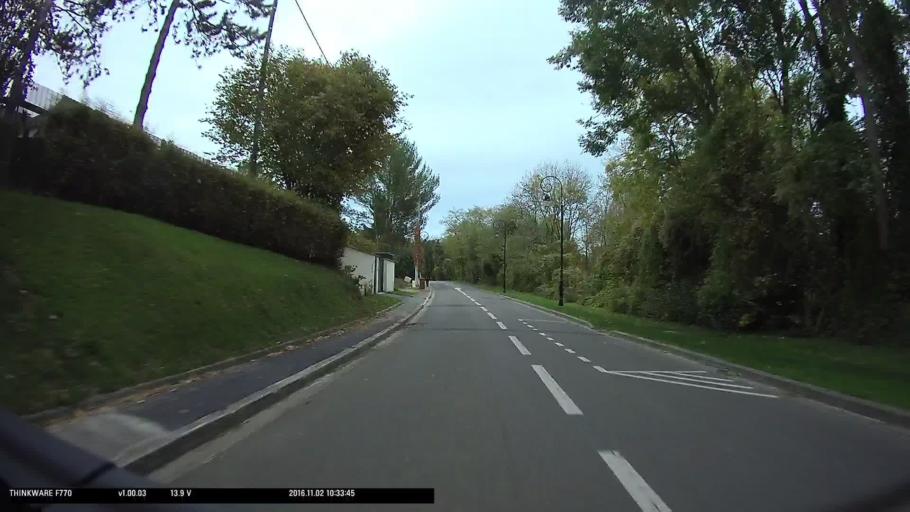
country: FR
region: Ile-de-France
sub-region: Departement du Val-d'Oise
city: Ableiges
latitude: 49.0886
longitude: 1.9887
